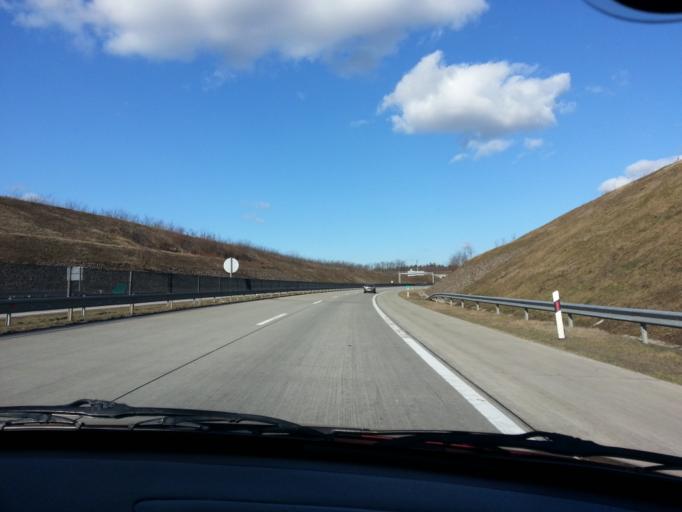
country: HU
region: Pest
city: Kerepes
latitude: 47.5856
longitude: 19.3123
